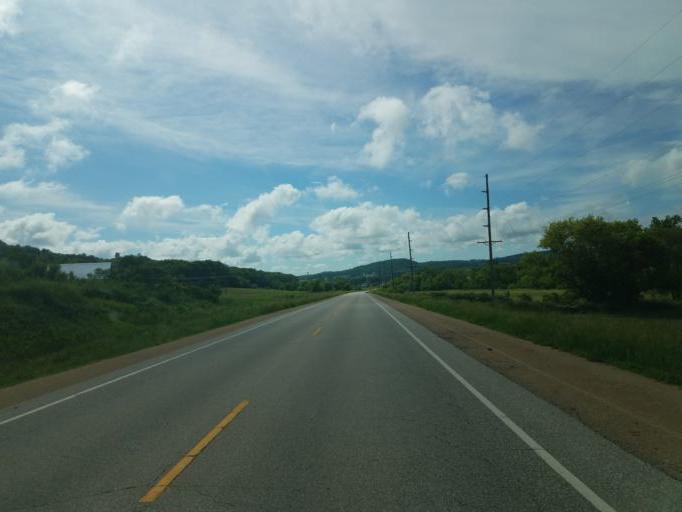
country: US
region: Wisconsin
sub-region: Monroe County
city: Tomah
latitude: 43.8275
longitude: -90.4580
